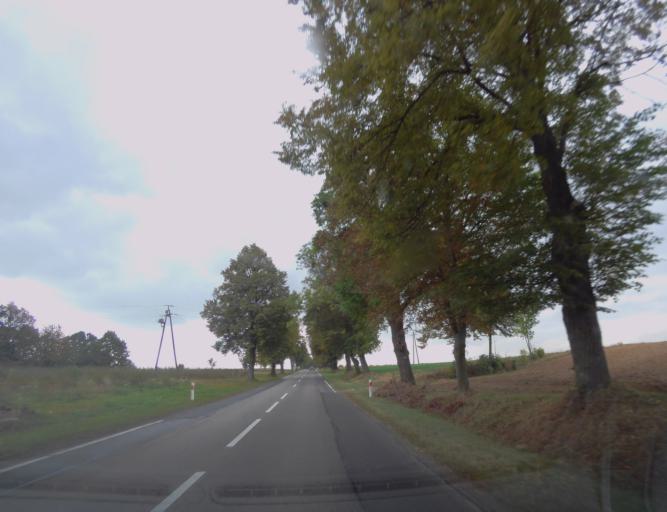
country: PL
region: Lublin Voivodeship
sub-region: Powiat krasnostawski
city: Zolkiewka
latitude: 50.9236
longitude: 22.8867
